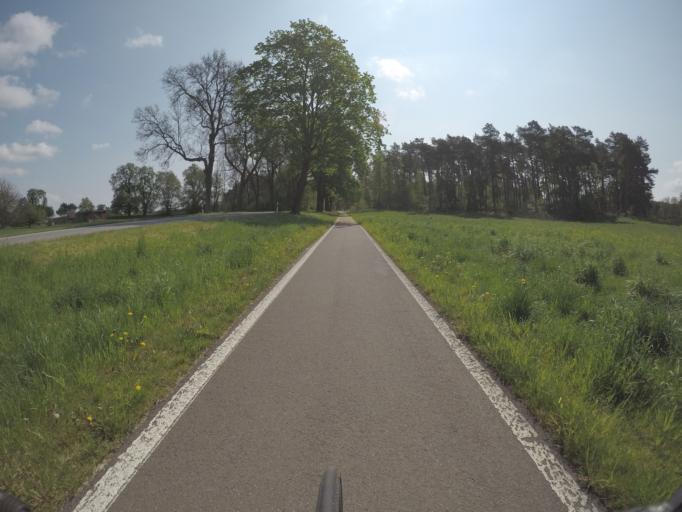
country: DE
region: Brandenburg
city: Wandlitz
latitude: 52.7966
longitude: 13.5152
